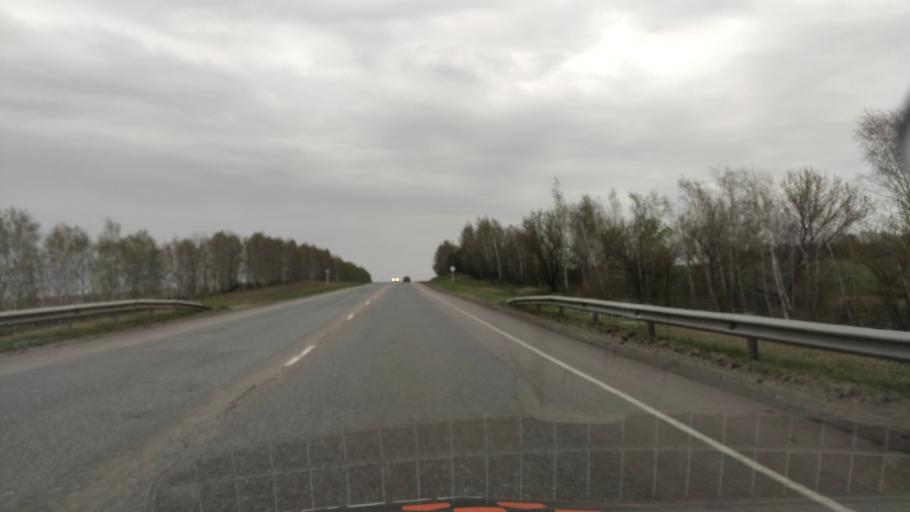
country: RU
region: Kursk
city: Gorshechnoye
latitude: 51.4495
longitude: 37.9148
